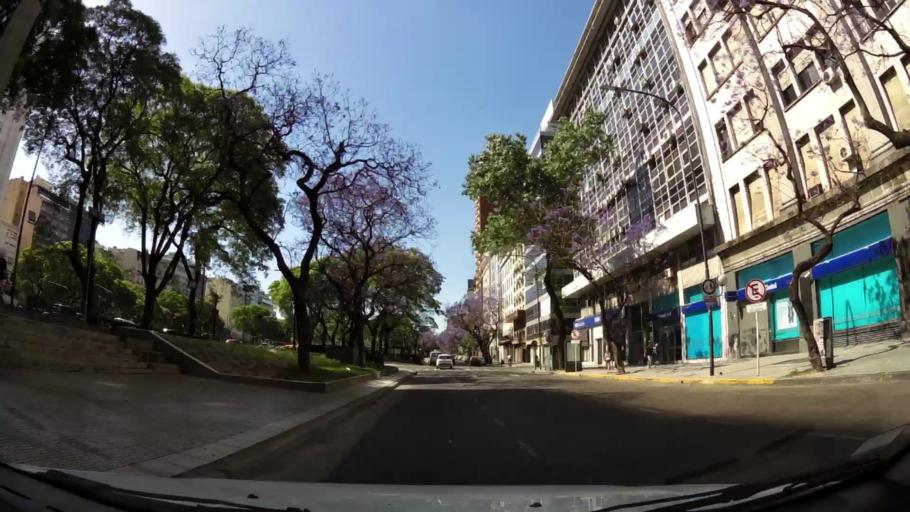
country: AR
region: Buenos Aires F.D.
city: Buenos Aires
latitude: -34.6123
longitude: -58.3805
